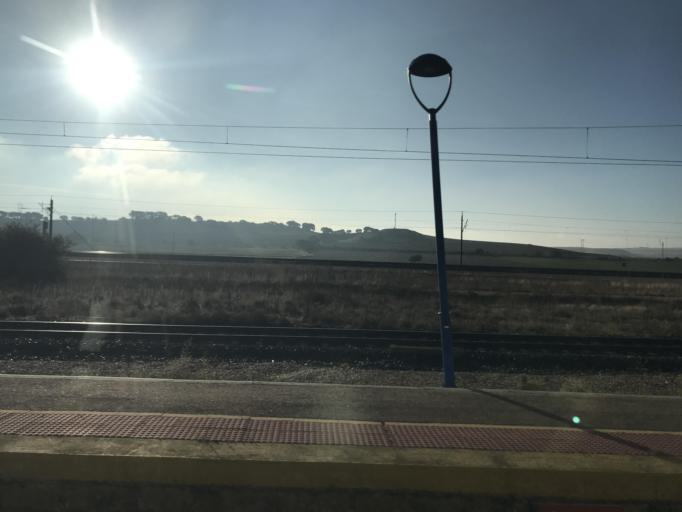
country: ES
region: Castille and Leon
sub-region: Provincia de Palencia
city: Quintana del Puente
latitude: 42.0804
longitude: -4.1977
